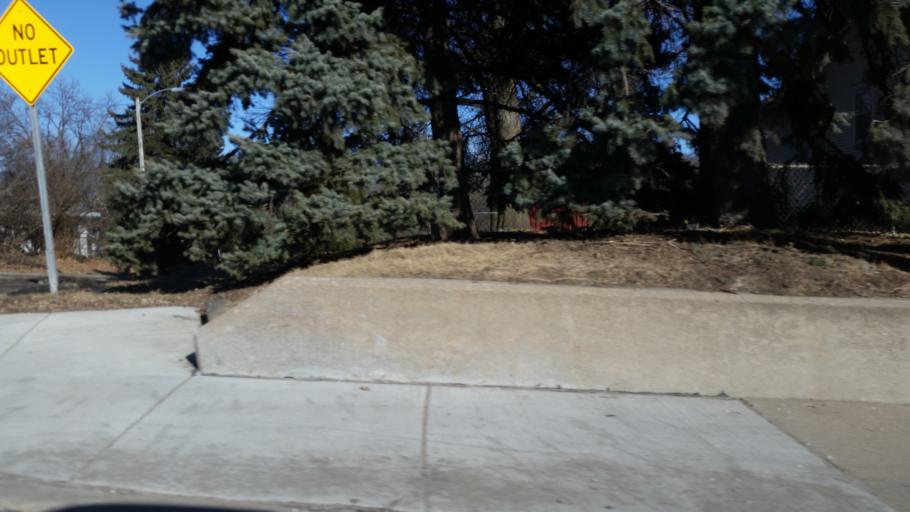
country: US
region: Nebraska
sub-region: Douglas County
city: Omaha
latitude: 41.1919
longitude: -95.9334
